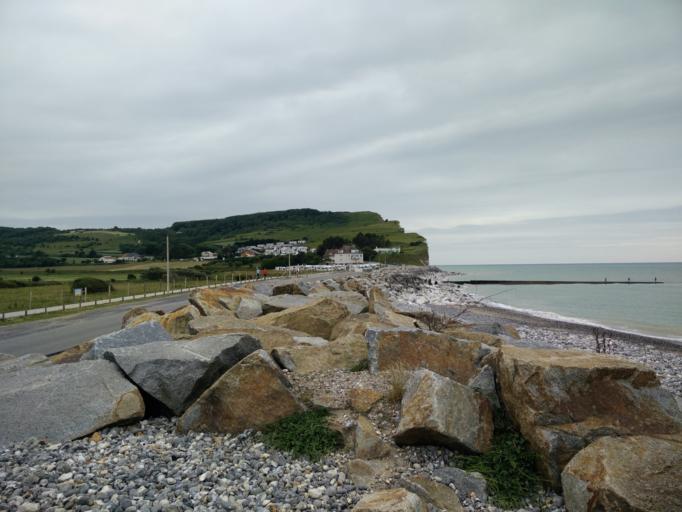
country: FR
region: Haute-Normandie
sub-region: Departement de la Seine-Maritime
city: Criel-sur-Mer
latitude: 50.0336
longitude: 1.3127
